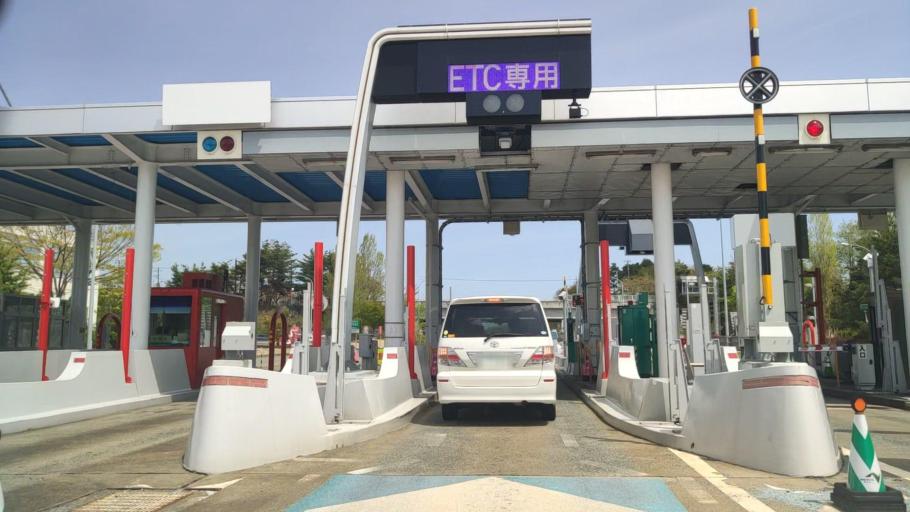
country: JP
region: Aomori
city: Hachinohe
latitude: 40.4862
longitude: 141.4626
